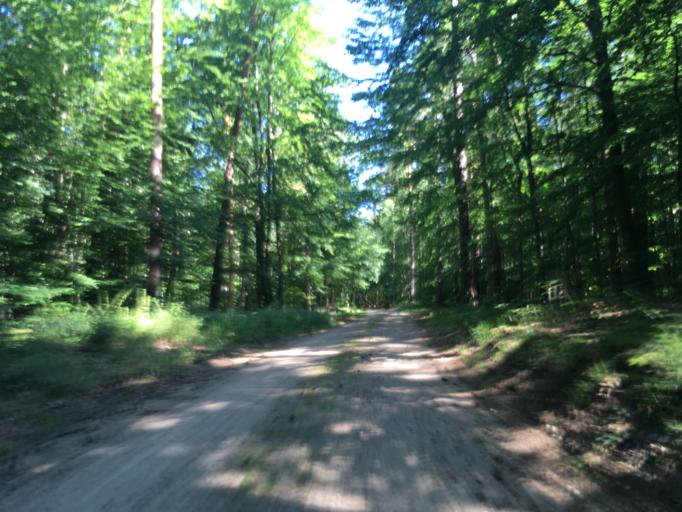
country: DE
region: Brandenburg
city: Furstenberg
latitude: 53.1692
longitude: 13.0520
